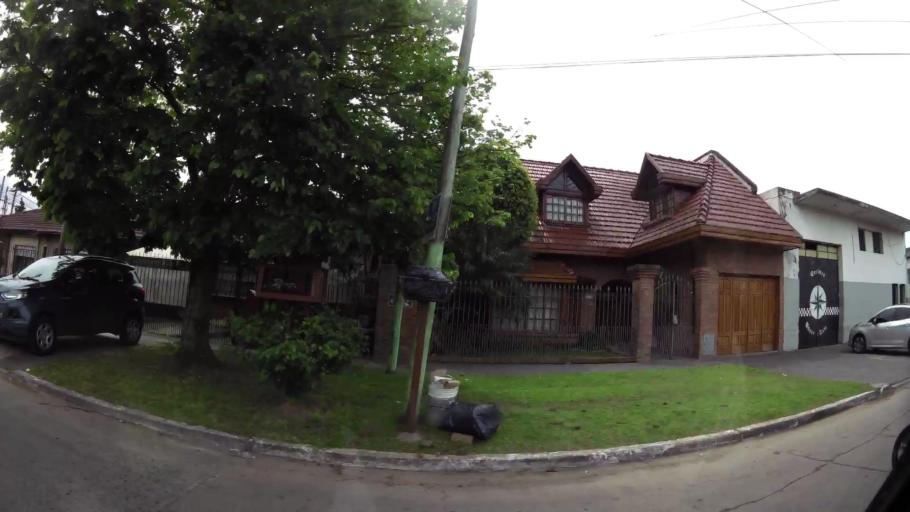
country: AR
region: Buenos Aires
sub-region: Partido de Quilmes
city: Quilmes
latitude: -34.7636
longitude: -58.2720
